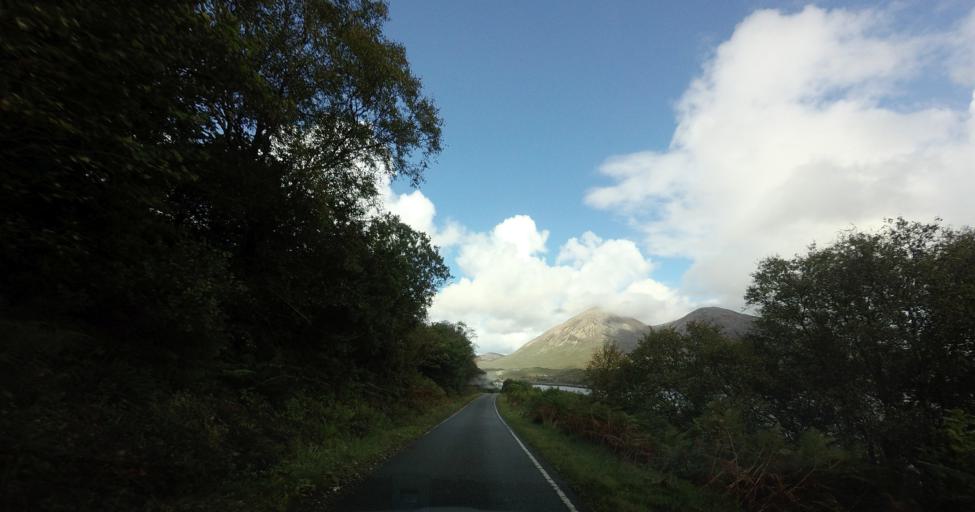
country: GB
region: Scotland
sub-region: Highland
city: Portree
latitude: 57.1974
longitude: -6.0280
